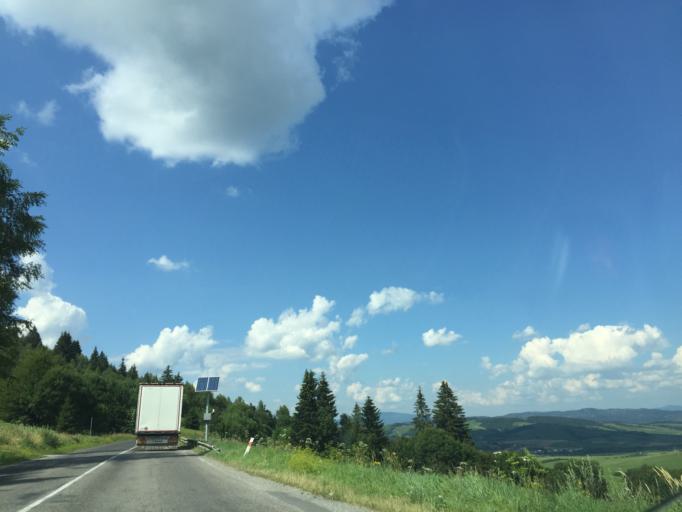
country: SK
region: Zilinsky
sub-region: Okres Dolny Kubin
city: Dolny Kubin
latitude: 49.3038
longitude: 19.3536
